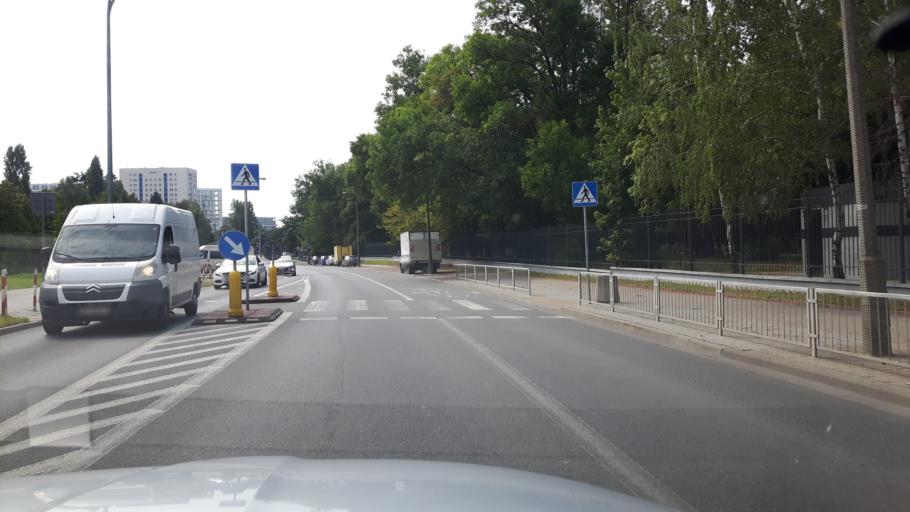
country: PL
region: Masovian Voivodeship
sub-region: Warszawa
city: Ochota
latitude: 52.2316
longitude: 20.9489
